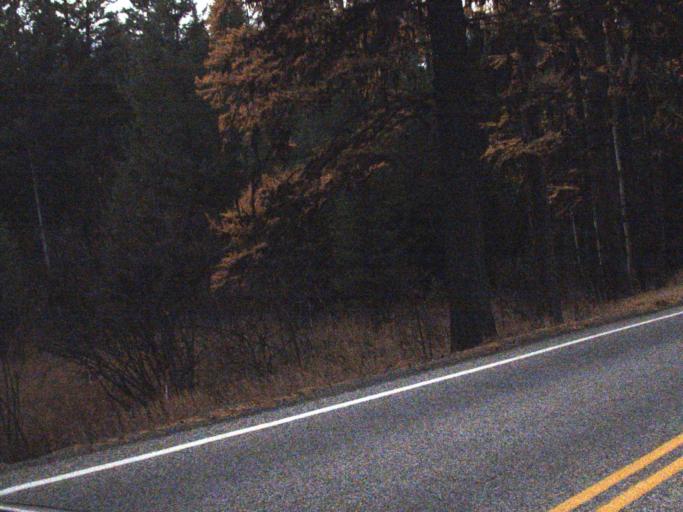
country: US
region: Washington
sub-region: Ferry County
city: Republic
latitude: 48.6005
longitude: -118.6532
